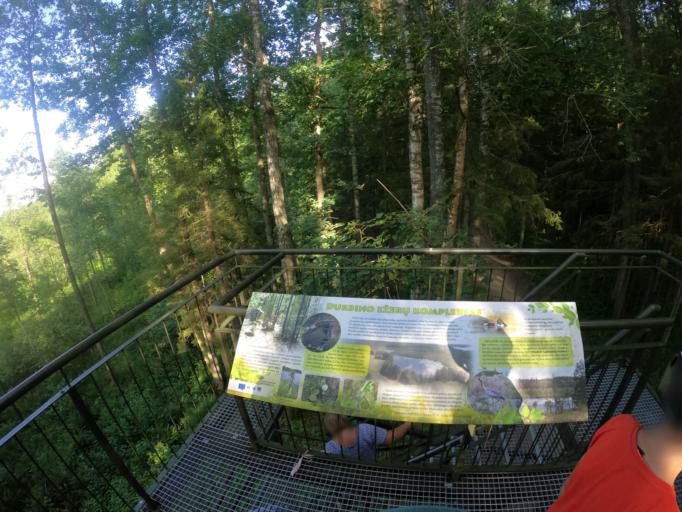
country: LT
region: Telsiu apskritis
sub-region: Telsiai
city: Telsiai
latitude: 55.9786
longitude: 22.1678
